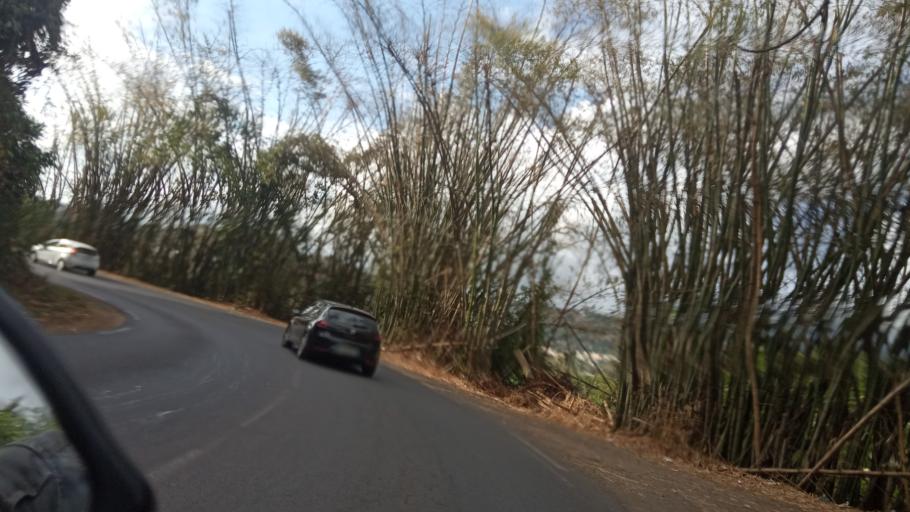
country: YT
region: Dembeni
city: Dembeni
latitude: -12.8374
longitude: 45.1827
